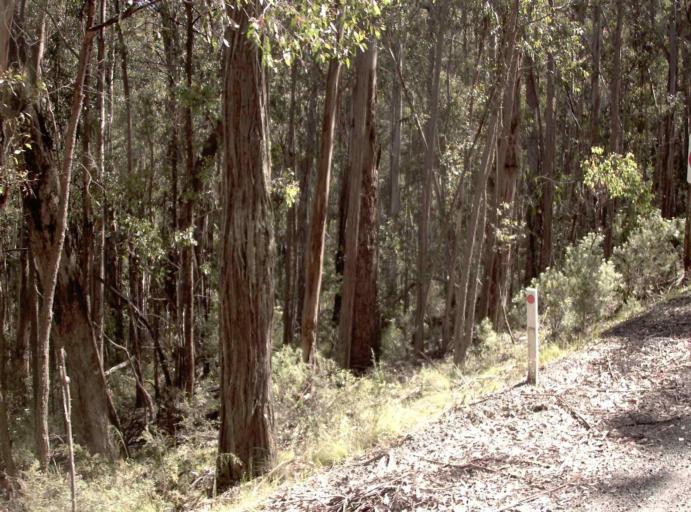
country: AU
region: New South Wales
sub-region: Bombala
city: Bombala
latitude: -37.2670
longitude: 148.7247
